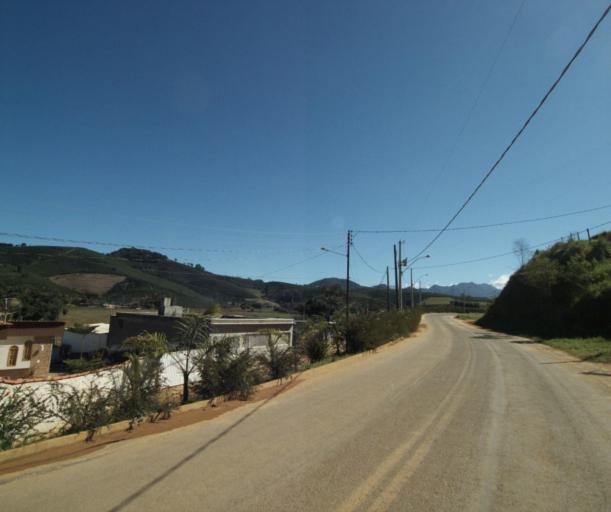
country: BR
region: Minas Gerais
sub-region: Espera Feliz
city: Espera Feliz
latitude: -20.6863
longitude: -41.8423
